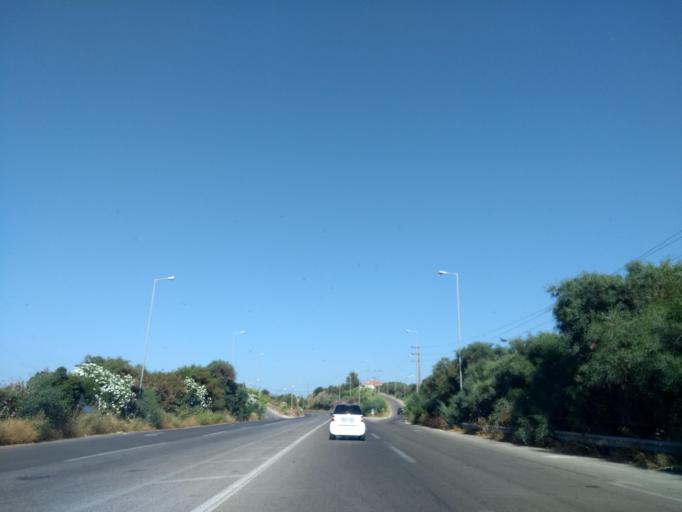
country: GR
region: Crete
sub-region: Nomos Chanias
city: Galatas
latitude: 35.5050
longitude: 23.9568
